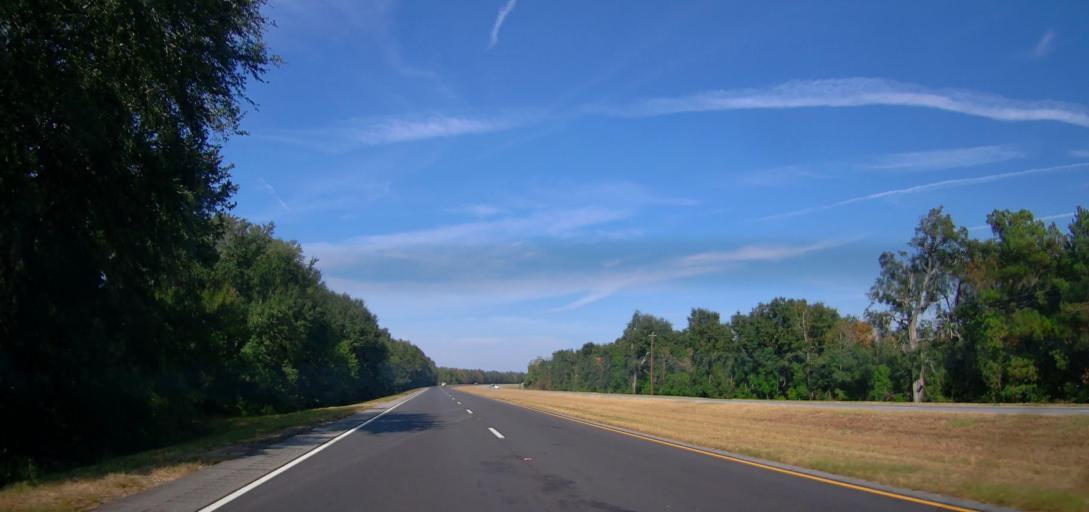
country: US
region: Georgia
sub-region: Dougherty County
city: Putney
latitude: 31.3968
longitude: -84.1462
